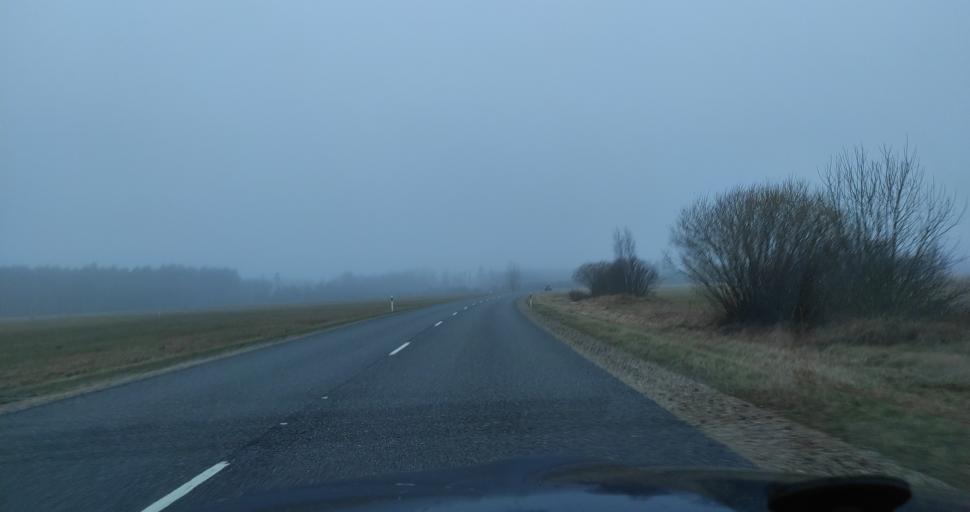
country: LV
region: Pavilostas
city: Pavilosta
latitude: 56.9538
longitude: 21.3161
